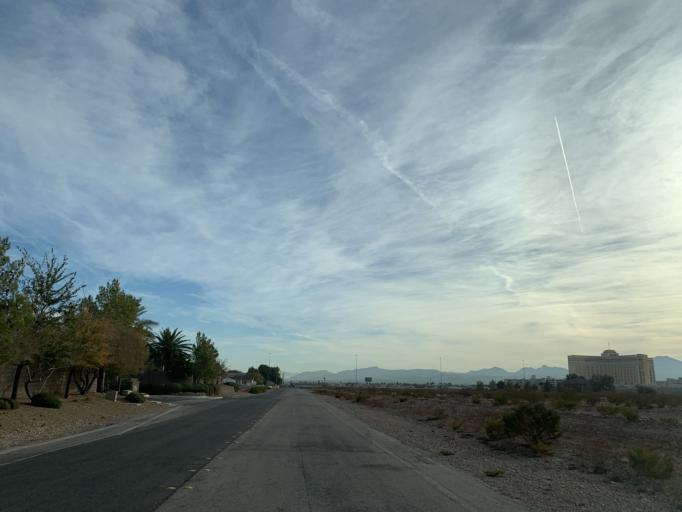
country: US
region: Nevada
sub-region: Clark County
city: Enterprise
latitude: 36.0172
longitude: -115.1878
